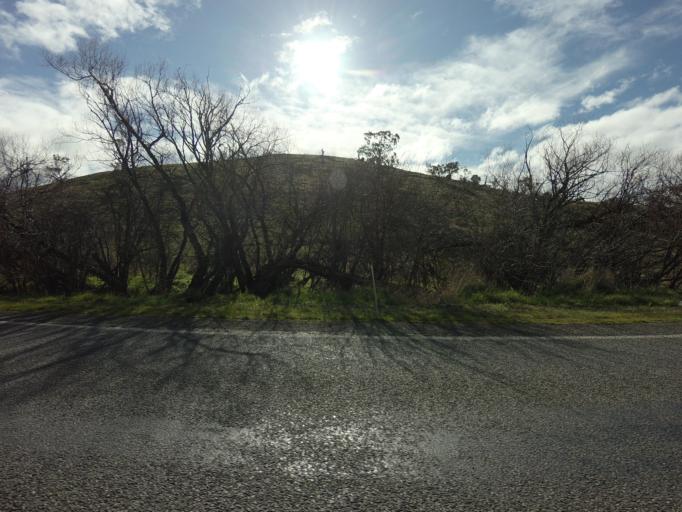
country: AU
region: Tasmania
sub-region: Derwent Valley
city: New Norfolk
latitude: -42.6265
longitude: 146.9011
